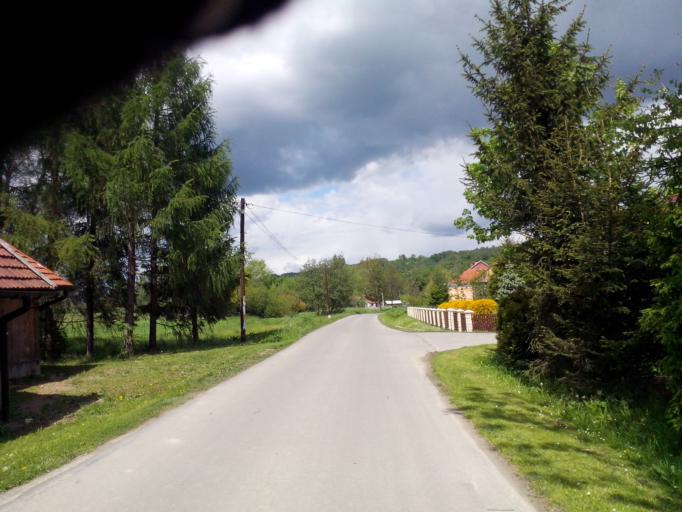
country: PL
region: Subcarpathian Voivodeship
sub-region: Powiat strzyzowski
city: Strzyzow
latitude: 49.8349
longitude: 21.8352
